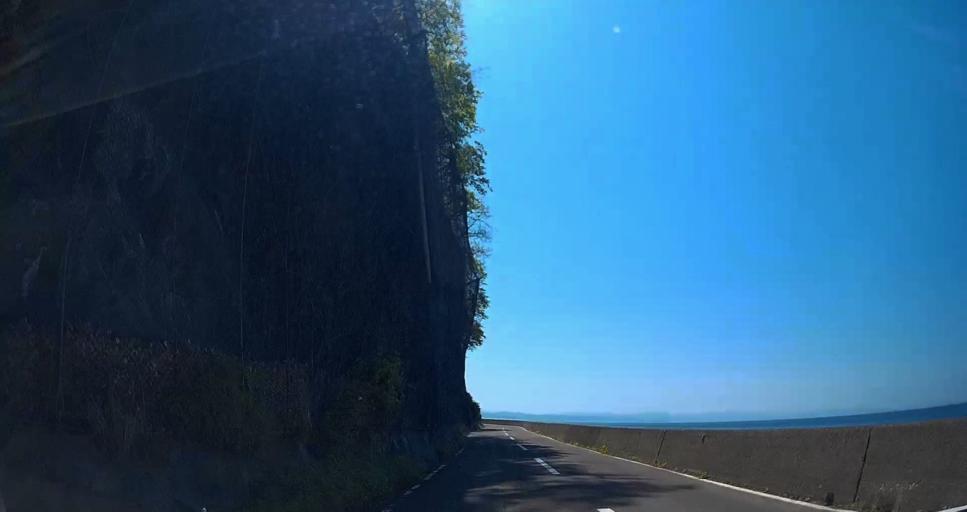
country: JP
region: Aomori
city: Aomori Shi
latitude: 41.1354
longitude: 140.7778
